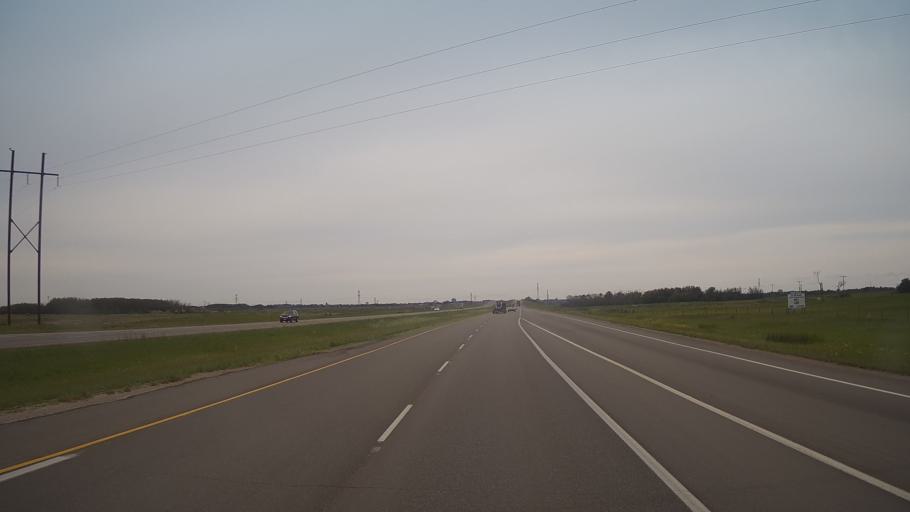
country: CA
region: Saskatchewan
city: Saskatoon
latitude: 52.0592
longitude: -106.6001
